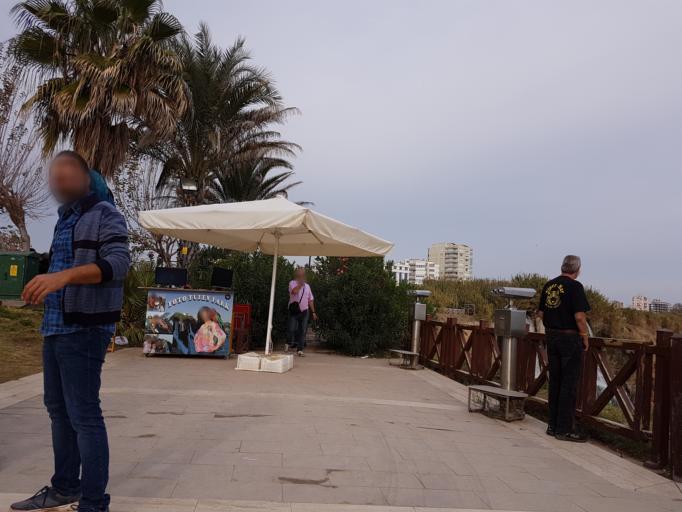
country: TR
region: Antalya
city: Antalya
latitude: 36.8502
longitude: 30.7823
